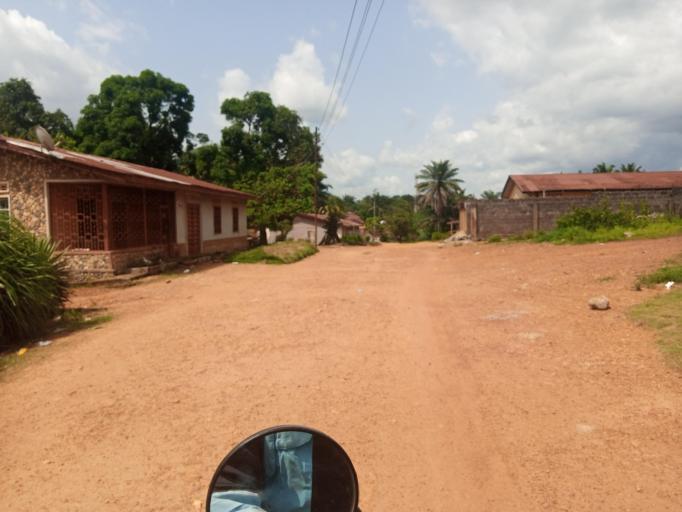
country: SL
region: Southern Province
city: Bo
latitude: 7.9766
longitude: -11.7320
